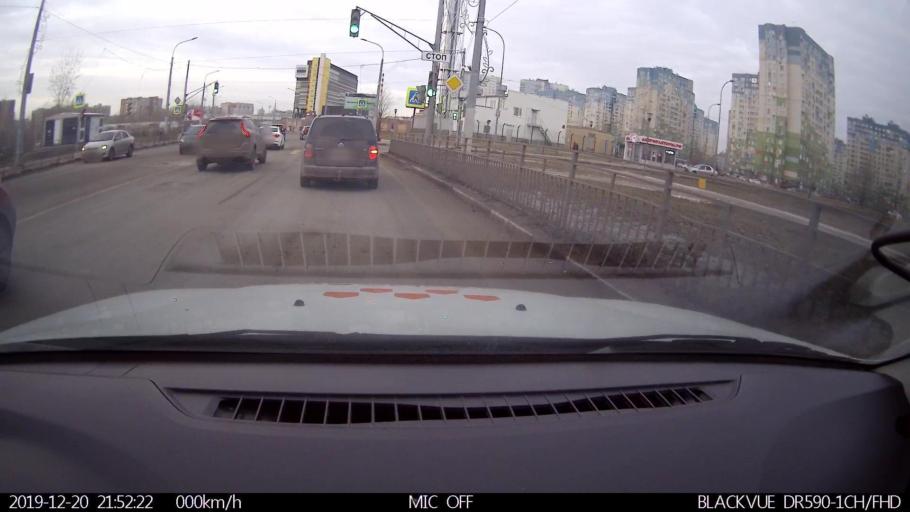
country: RU
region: Nizjnij Novgorod
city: Nizhniy Novgorod
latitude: 56.3379
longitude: 43.9527
